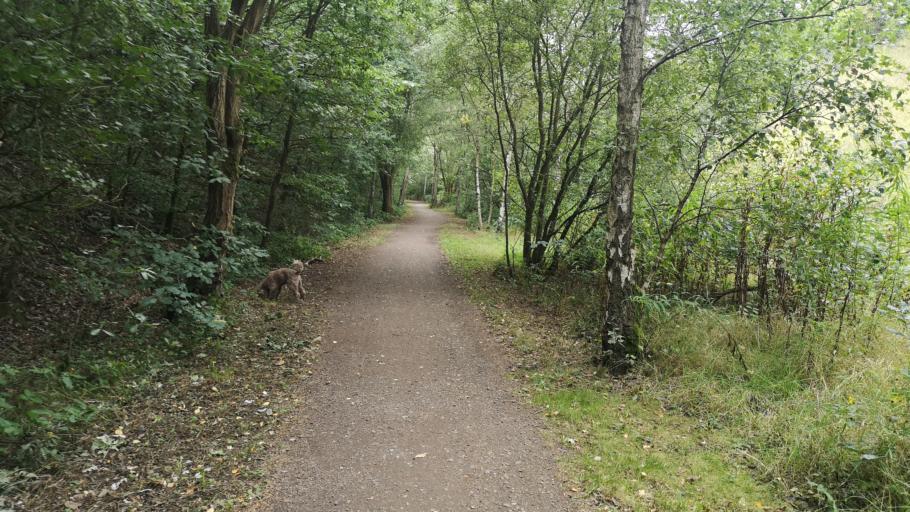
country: GB
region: England
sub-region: Barnsley
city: Royston
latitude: 53.6177
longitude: -1.4535
